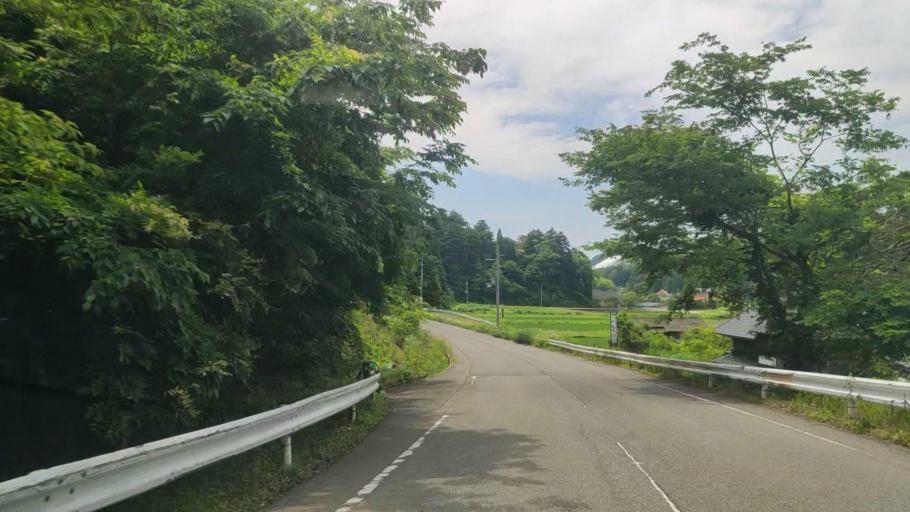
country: JP
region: Hyogo
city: Toyooka
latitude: 35.5067
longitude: 134.6855
